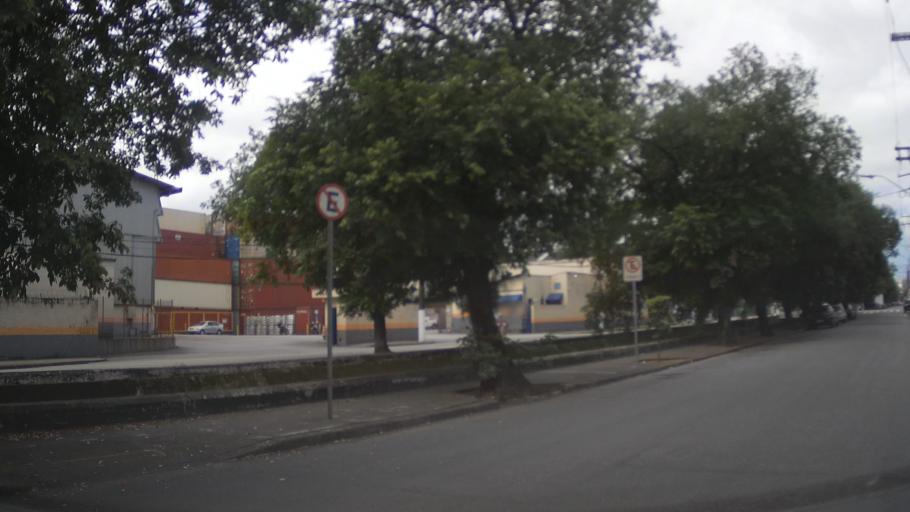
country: BR
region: Sao Paulo
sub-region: Santos
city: Santos
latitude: -23.9604
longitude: -46.3150
